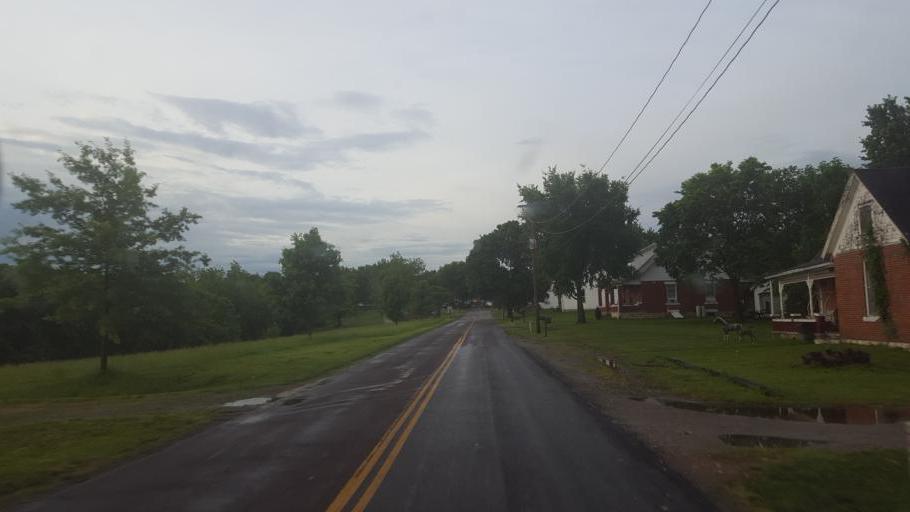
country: US
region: Missouri
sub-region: Moniteau County
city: California
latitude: 38.6417
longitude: -92.5682
